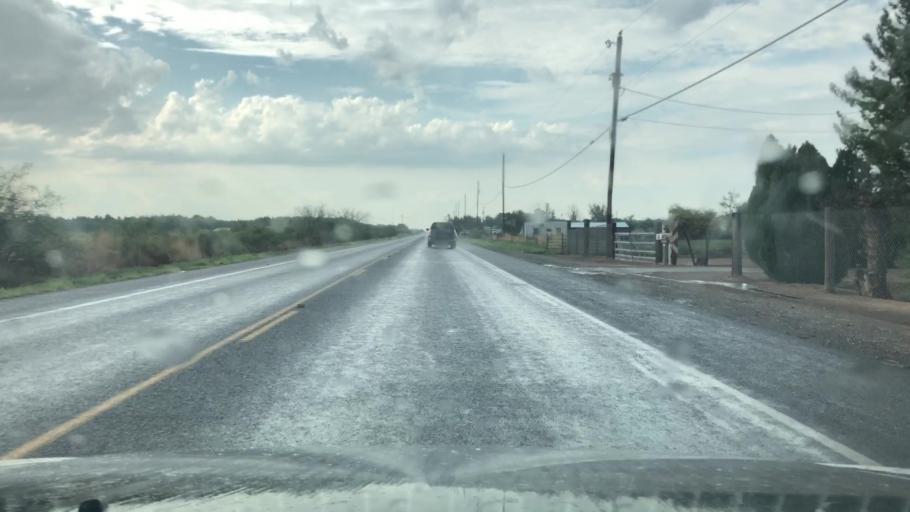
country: US
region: New Mexico
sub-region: Dona Ana County
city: Mesquite
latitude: 32.1886
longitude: -106.7117
